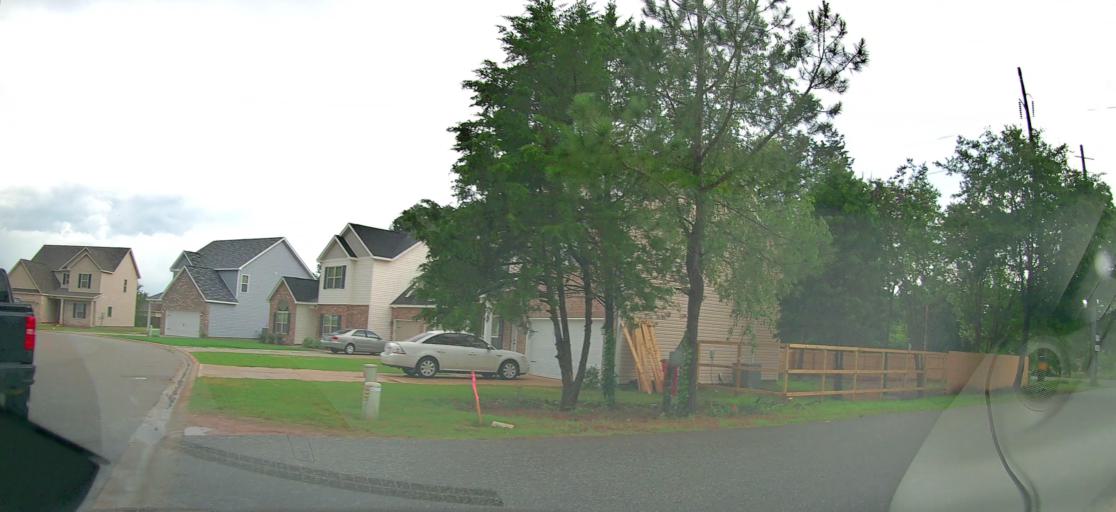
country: US
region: Georgia
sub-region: Houston County
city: Centerville
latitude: 32.6503
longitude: -83.7082
